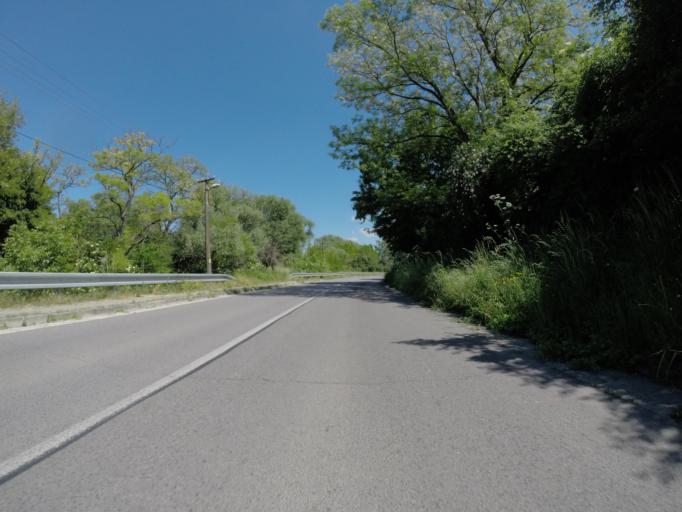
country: SK
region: Nitriansky
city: Banovce nad Bebravou
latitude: 48.5323
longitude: 18.1378
